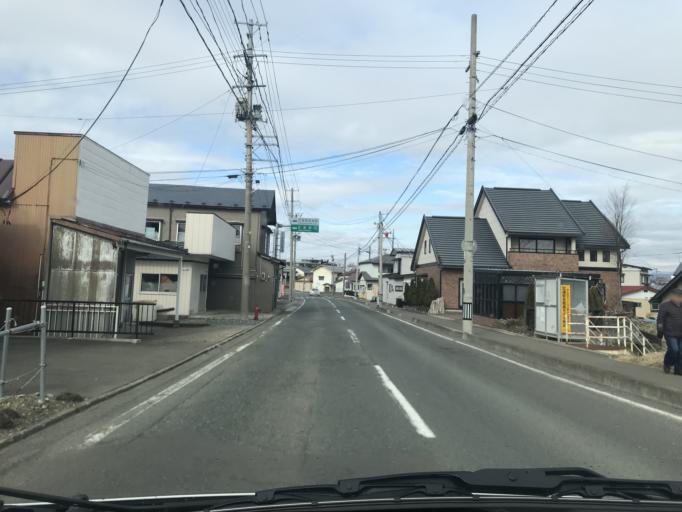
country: JP
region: Iwate
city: Hanamaki
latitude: 39.3800
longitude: 141.1066
